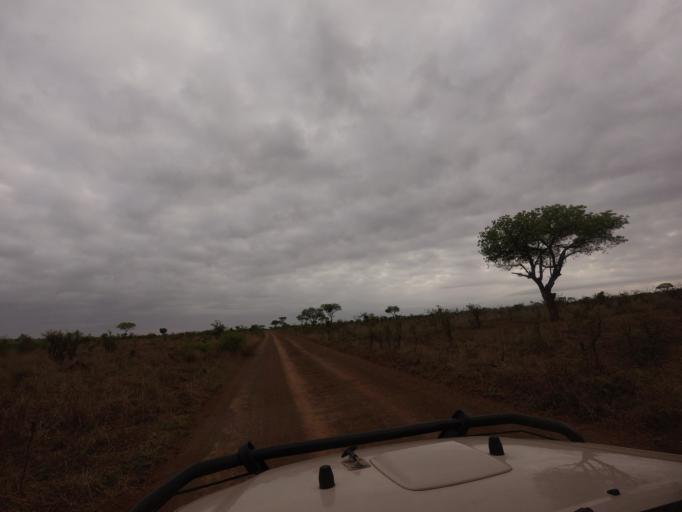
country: ZA
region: Mpumalanga
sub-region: Ehlanzeni District
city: Komatipoort
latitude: -25.3100
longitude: 31.9137
